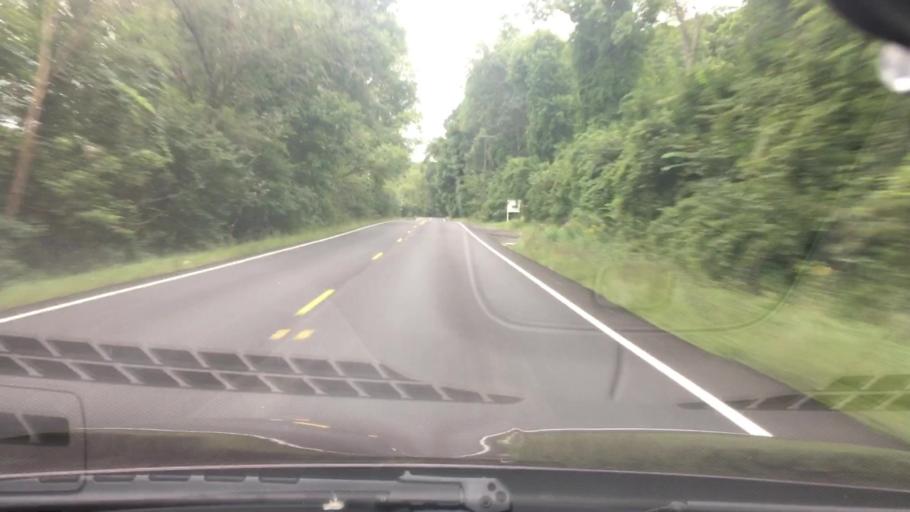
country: US
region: New York
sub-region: Dutchess County
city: Dover Plains
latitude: 41.8635
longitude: -73.5067
